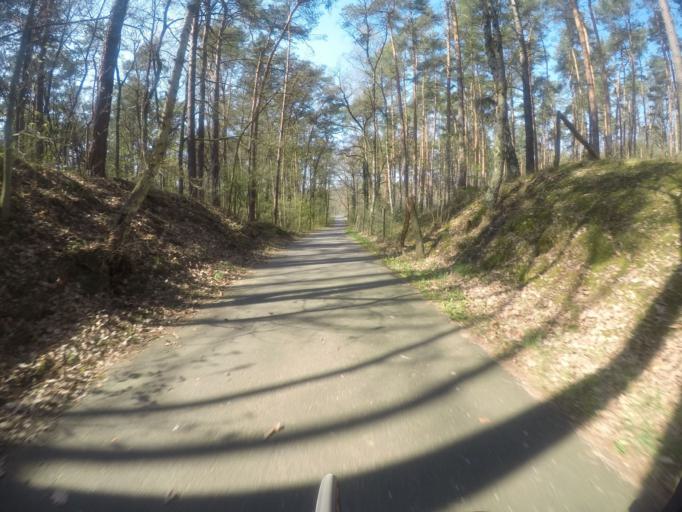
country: DE
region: Brandenburg
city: Brieselang
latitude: 52.6439
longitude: 13.0336
